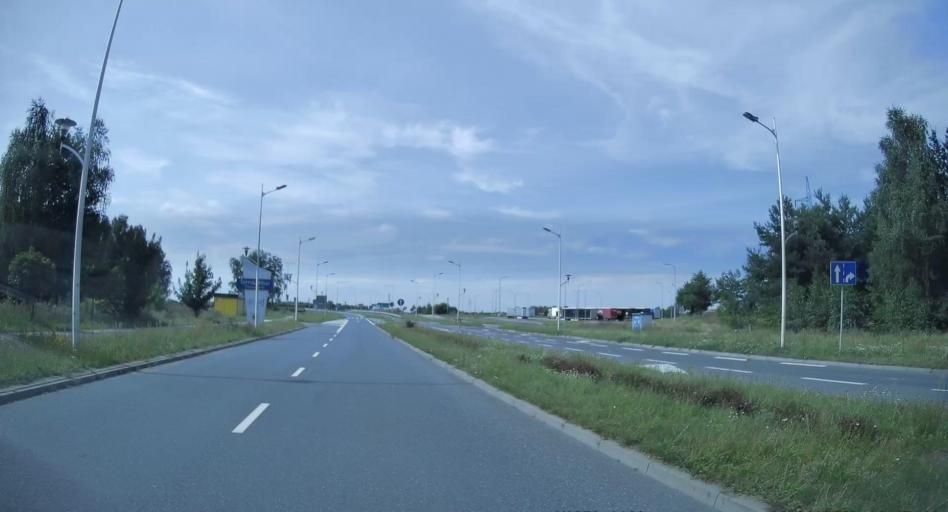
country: PL
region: Lodz Voivodeship
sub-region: Powiat tomaszowski
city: Tomaszow Mazowiecki
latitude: 51.5462
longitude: 19.9923
